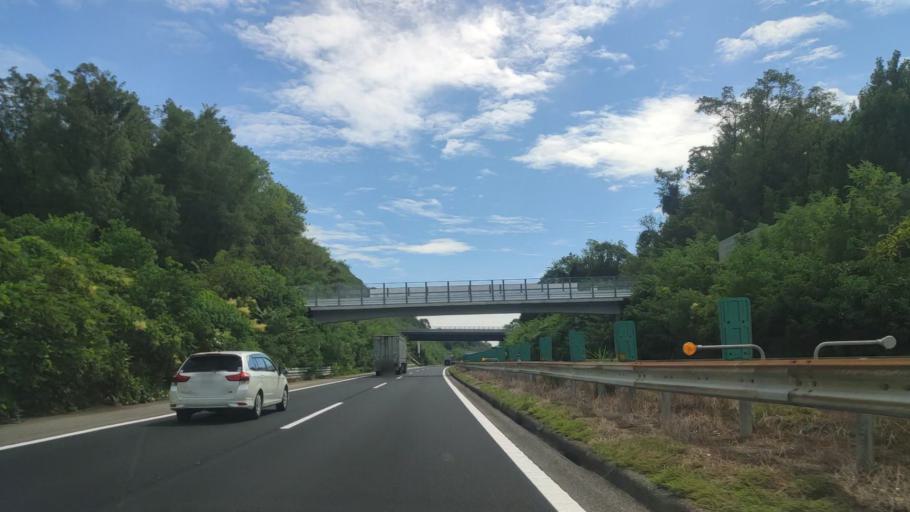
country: JP
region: Aichi
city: Okazaki
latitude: 34.9591
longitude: 137.1926
